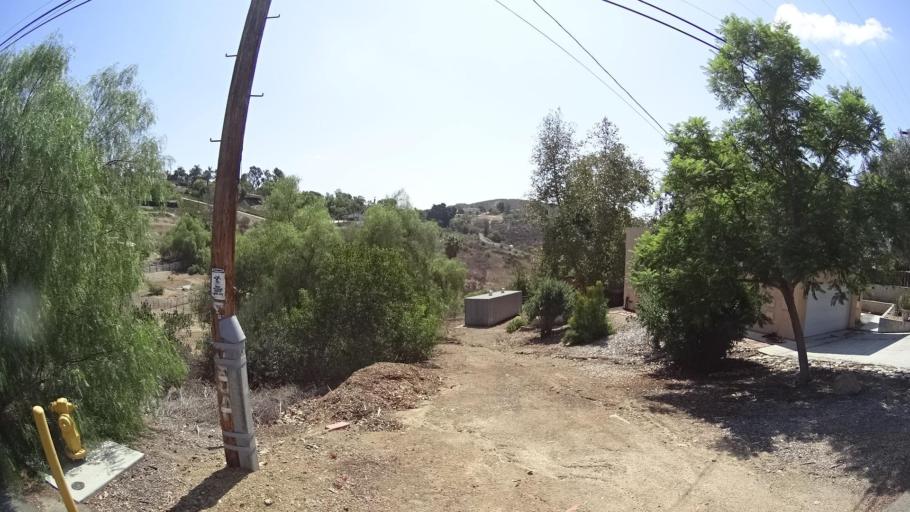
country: US
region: California
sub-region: San Diego County
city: Spring Valley
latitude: 32.7358
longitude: -116.9930
